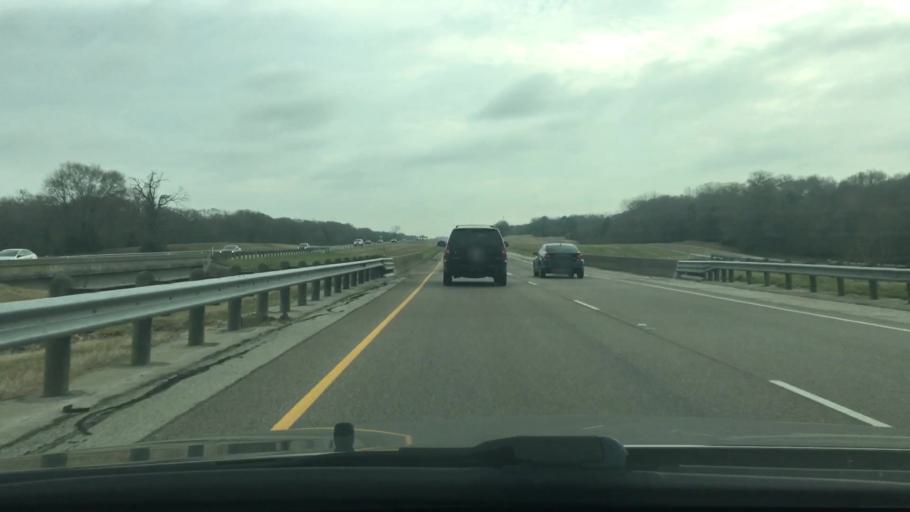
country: US
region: Texas
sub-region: Freestone County
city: Fairfield
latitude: 31.6273
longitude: -96.1578
